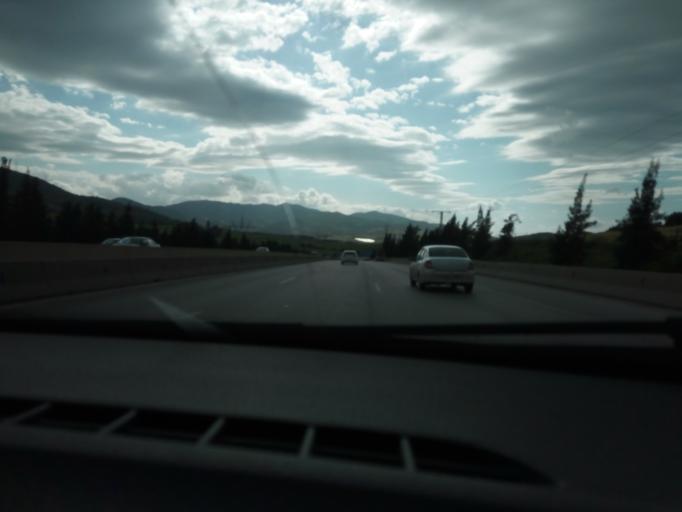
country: DZ
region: Tipaza
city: El Affroun
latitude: 36.4461
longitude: 2.6186
